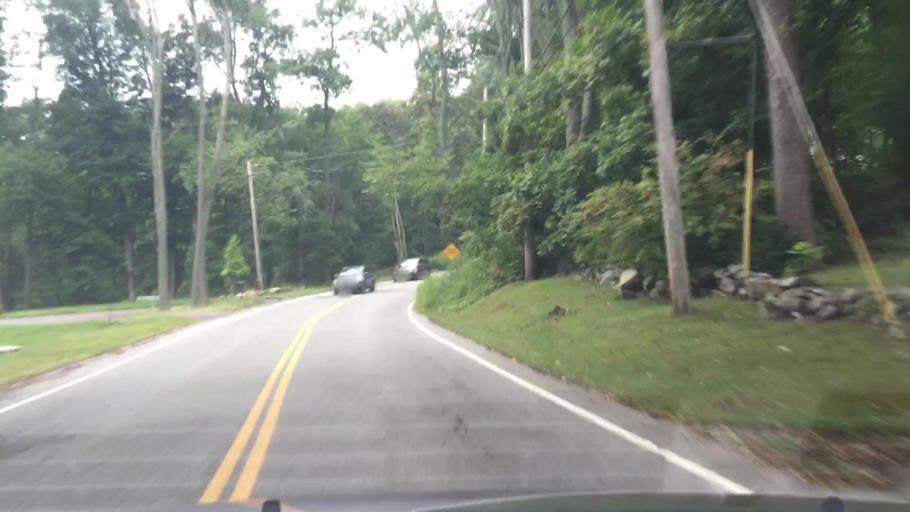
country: US
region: Massachusetts
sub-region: Essex County
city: North Andover
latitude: 42.7023
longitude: -71.0774
